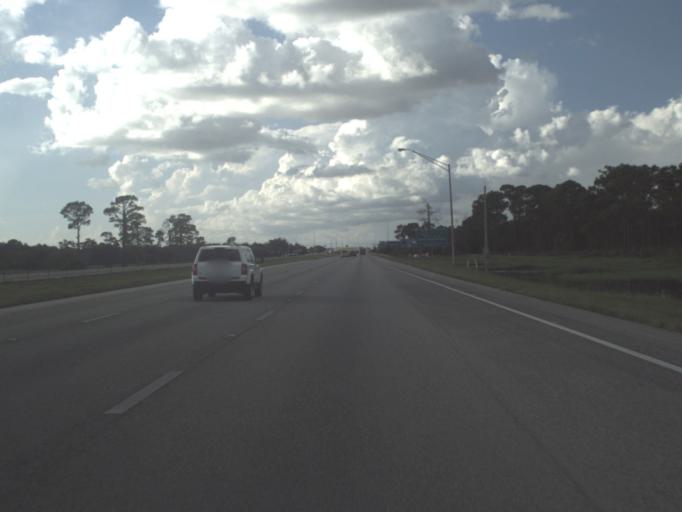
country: US
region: Florida
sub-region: Charlotte County
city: Charlotte Park
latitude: 26.8857
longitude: -81.9919
